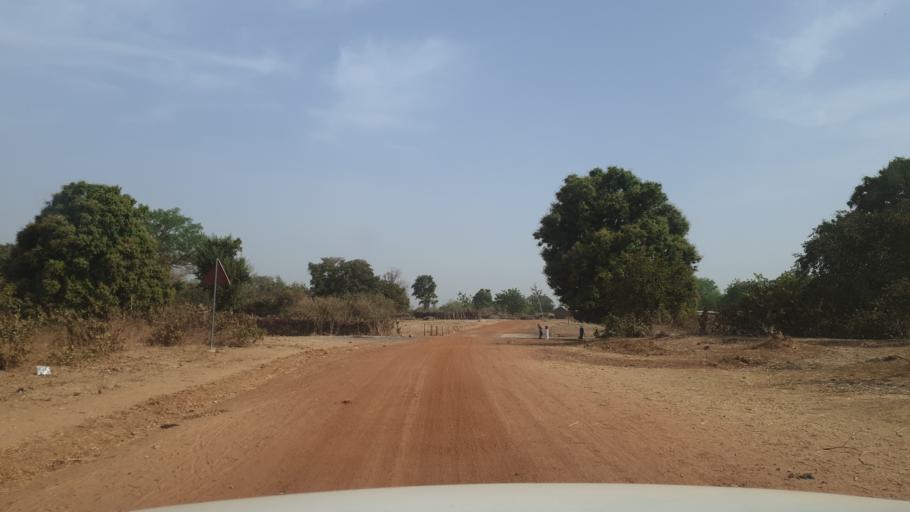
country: ML
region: Koulikoro
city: Kolokani
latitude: 13.3181
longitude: -8.2770
